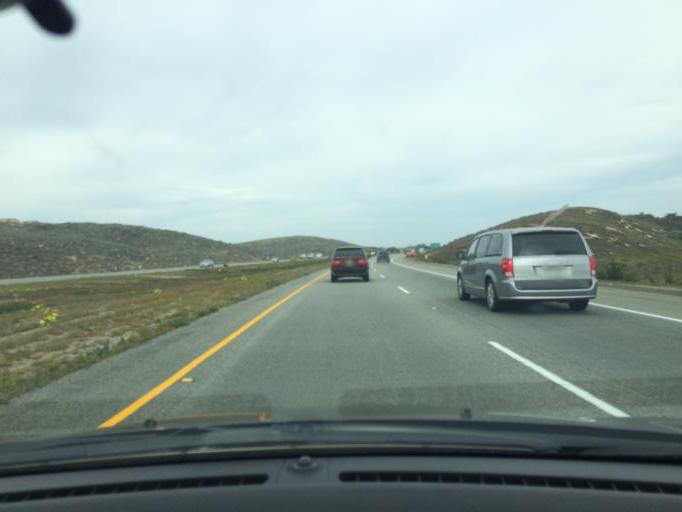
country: US
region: California
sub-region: Monterey County
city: Marina
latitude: 36.6889
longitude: -121.8085
